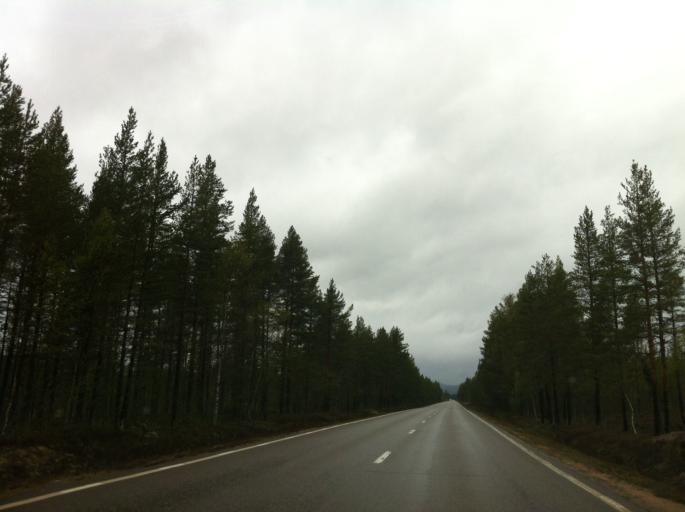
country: SE
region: Jaemtland
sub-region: Harjedalens Kommun
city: Sveg
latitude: 62.1349
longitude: 14.0064
